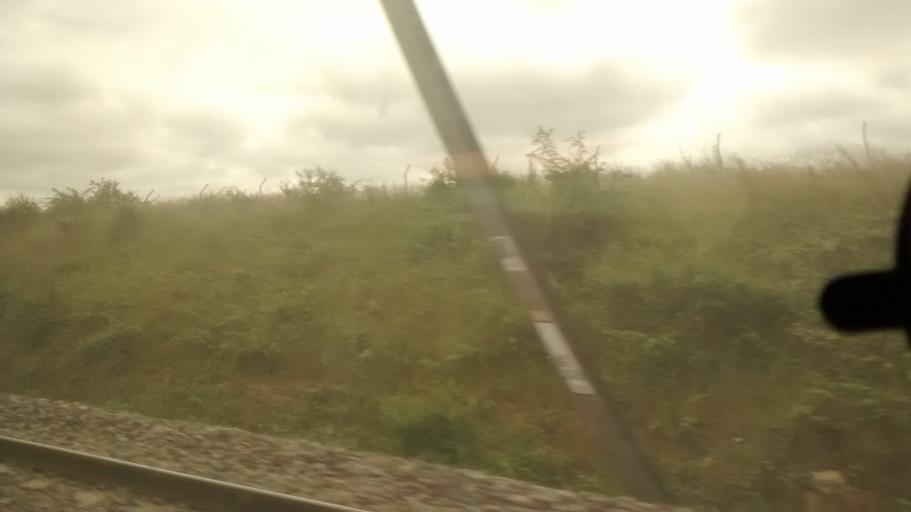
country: FR
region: Ile-de-France
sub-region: Departement des Yvelines
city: Ablis
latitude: 48.4825
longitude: 1.8712
